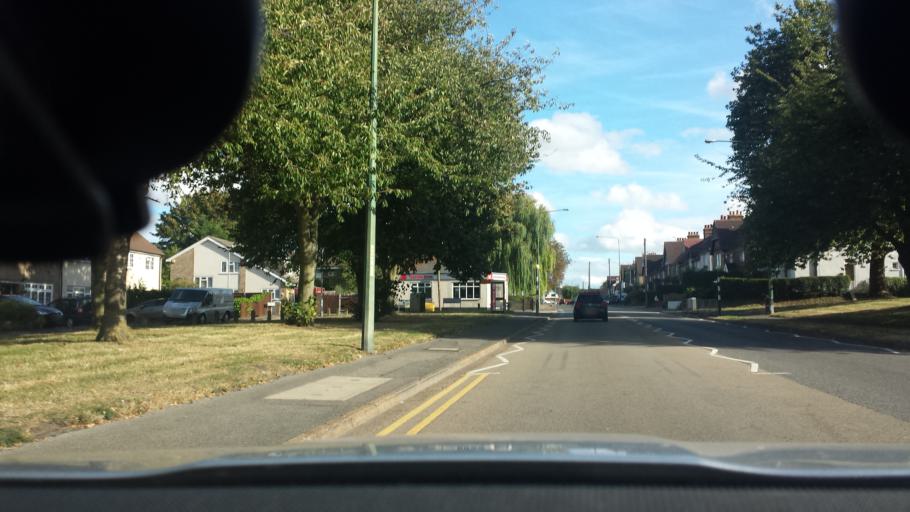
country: GB
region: England
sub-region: Kent
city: Swanley
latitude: 51.3931
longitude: 0.1835
